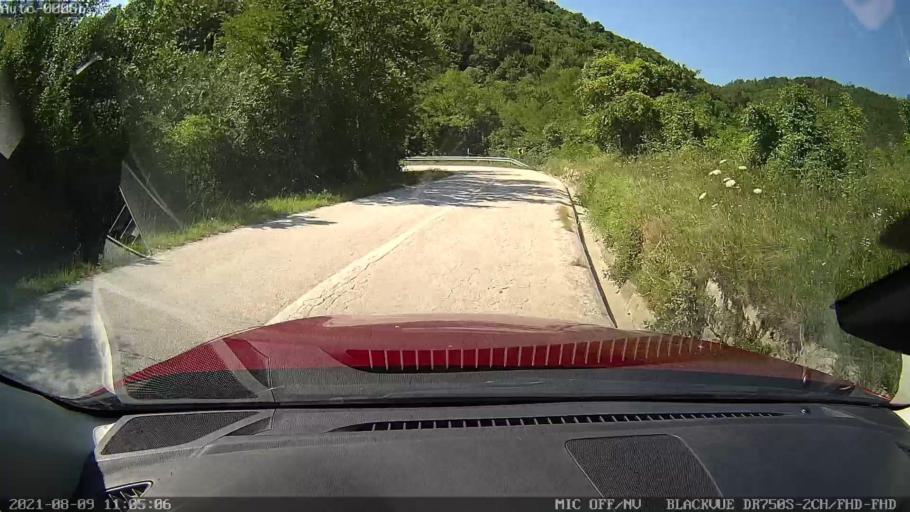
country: HR
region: Istarska
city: Lovran
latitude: 45.2874
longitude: 14.1152
